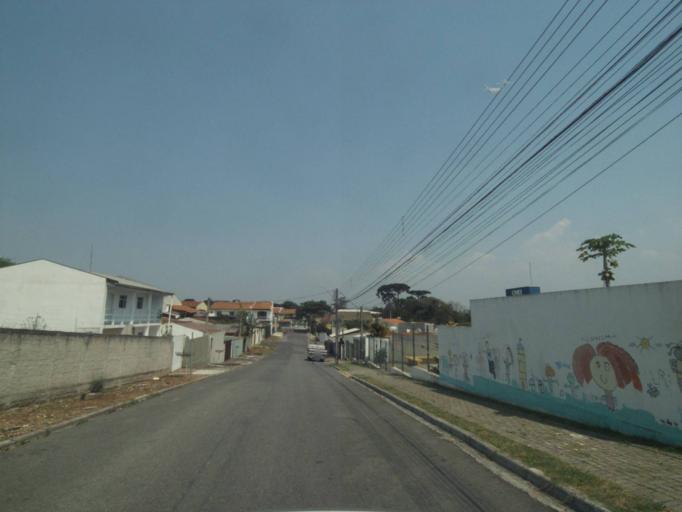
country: BR
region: Parana
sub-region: Sao Jose Dos Pinhais
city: Sao Jose dos Pinhais
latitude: -25.5433
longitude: -49.2443
